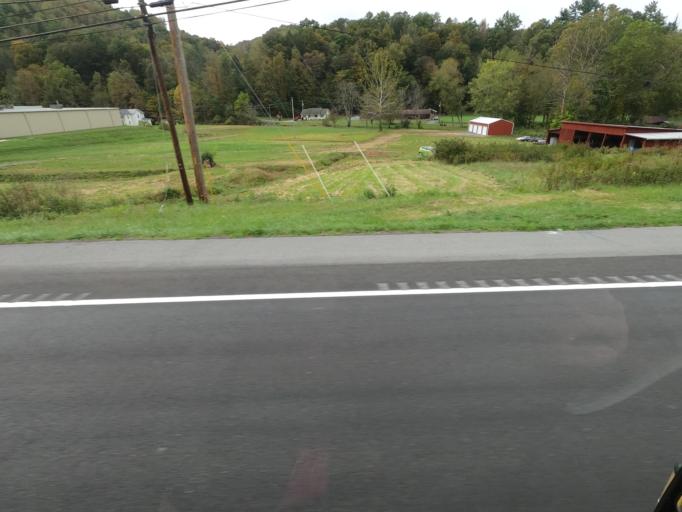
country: US
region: Tennessee
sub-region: Carter County
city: Elizabethton
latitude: 36.2386
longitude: -82.1882
